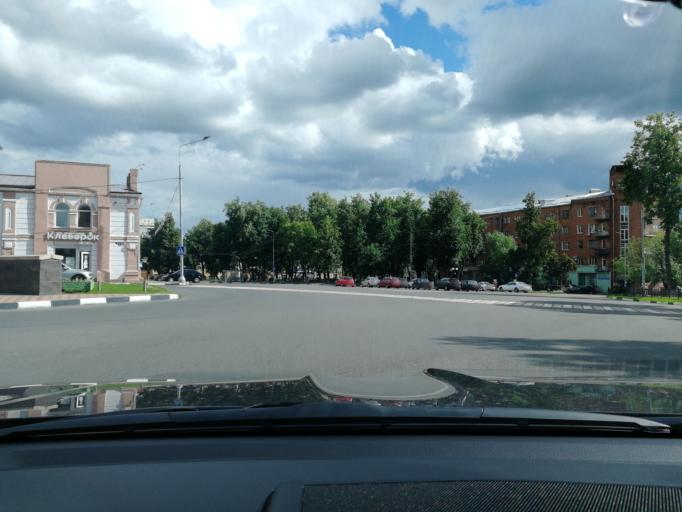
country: RU
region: Moskovskaya
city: Serpukhov
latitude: 54.9138
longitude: 37.4161
